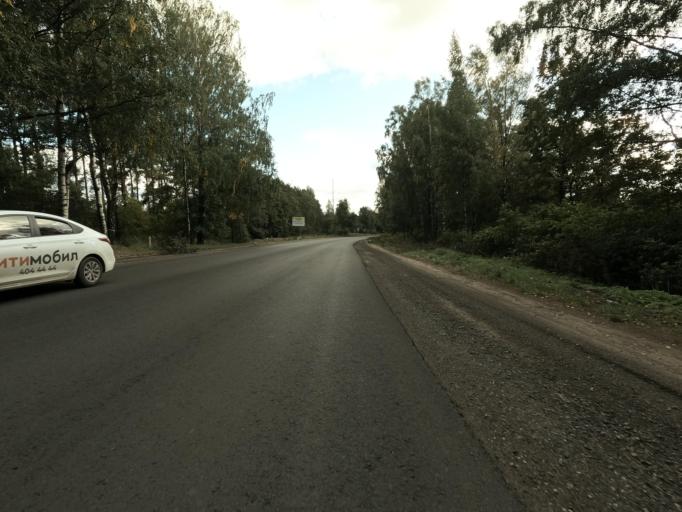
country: RU
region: Leningrad
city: Koltushi
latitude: 59.9487
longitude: 30.6575
